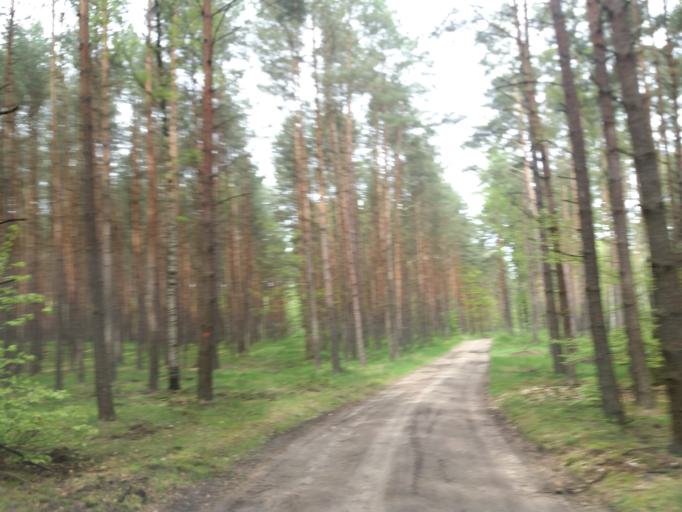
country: PL
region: Lubusz
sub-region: Powiat strzelecko-drezdenecki
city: Dobiegniew
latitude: 52.9961
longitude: 15.7222
